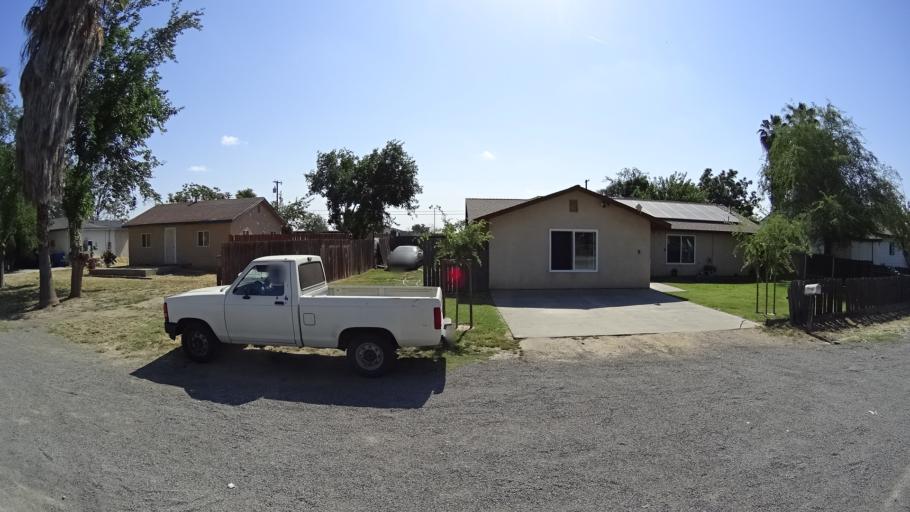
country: US
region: California
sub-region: Kings County
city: Home Garden
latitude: 36.3009
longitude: -119.6325
